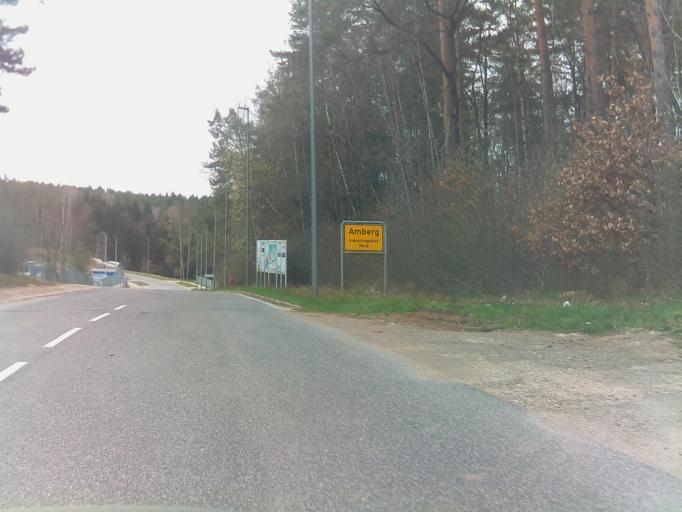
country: DE
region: Bavaria
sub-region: Upper Palatinate
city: Gebenbach
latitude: 49.4901
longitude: 11.8785
